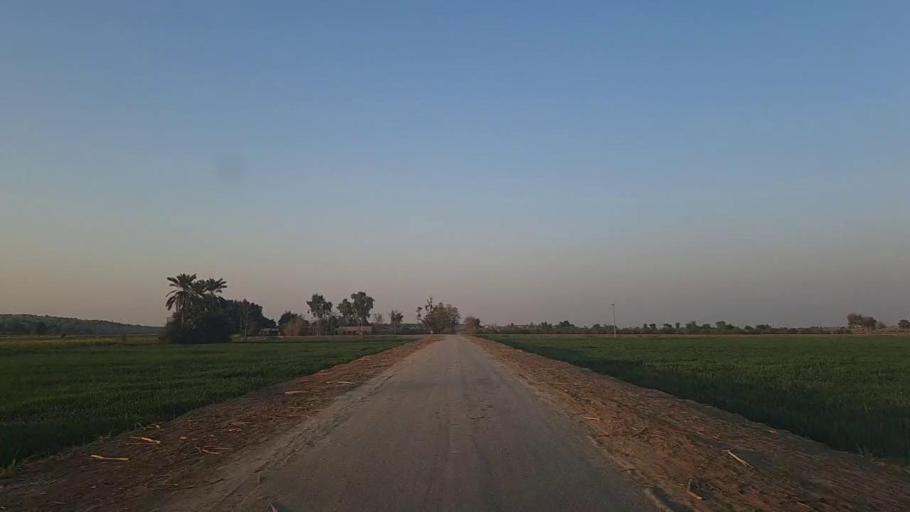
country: PK
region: Sindh
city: Jam Sahib
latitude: 26.3503
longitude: 68.7147
